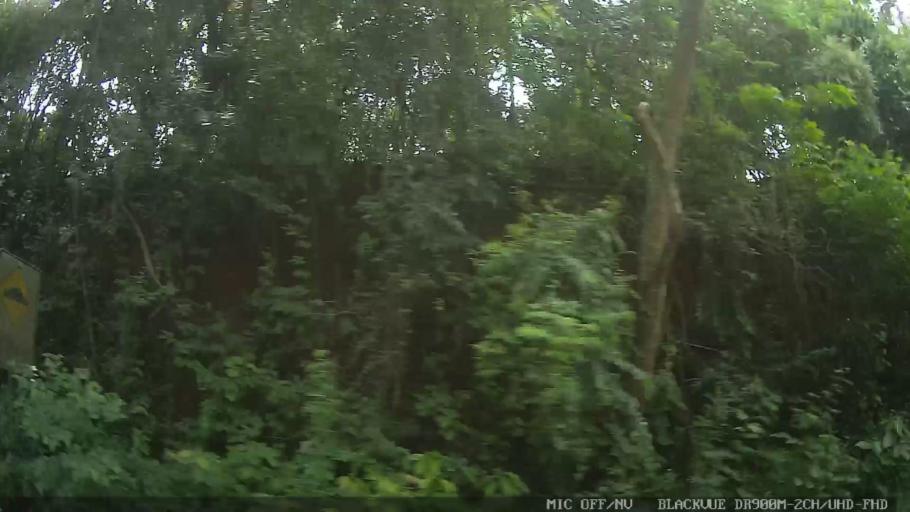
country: BR
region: Sao Paulo
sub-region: Suzano
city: Suzano
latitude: -23.4842
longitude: -46.2629
